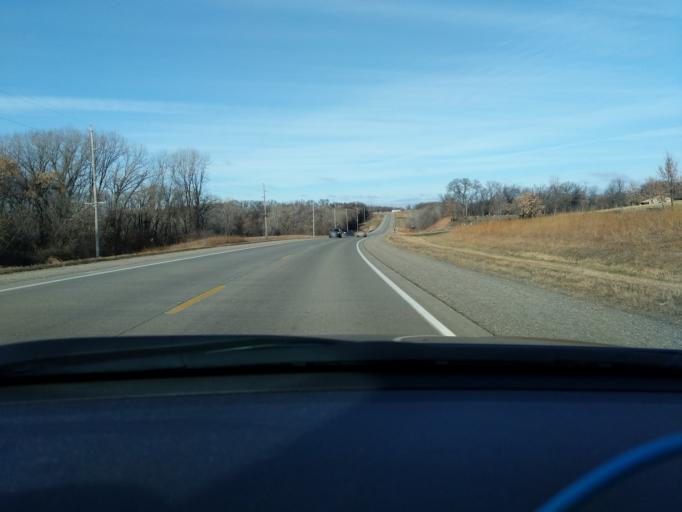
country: US
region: Minnesota
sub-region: Yellow Medicine County
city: Granite Falls
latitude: 44.7903
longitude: -95.4495
